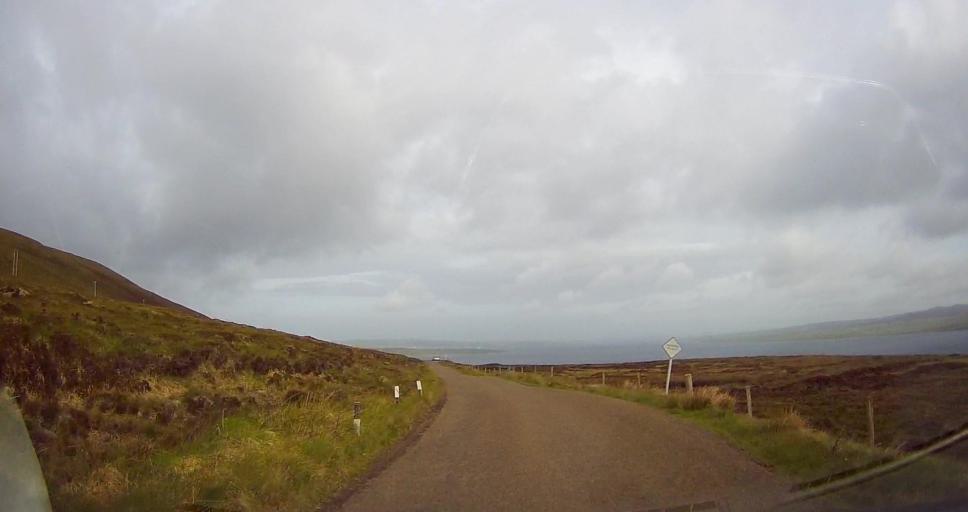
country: GB
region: Scotland
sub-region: Orkney Islands
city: Stromness
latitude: 58.8834
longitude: -3.2490
